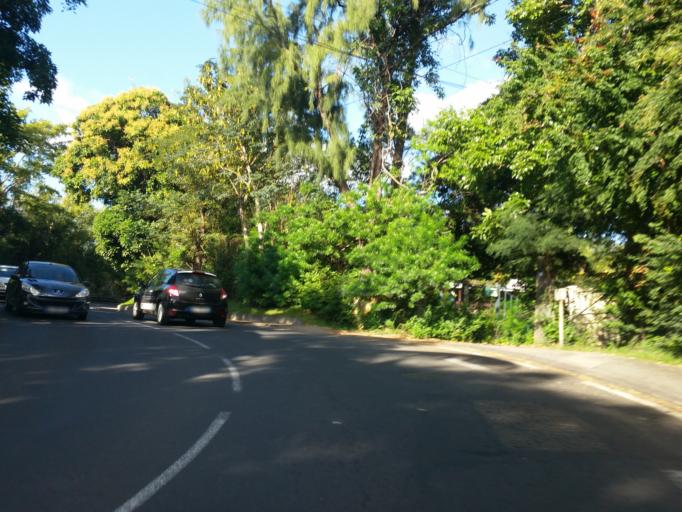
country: RE
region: Reunion
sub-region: Reunion
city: Sainte-Marie
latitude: -20.9085
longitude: 55.5032
